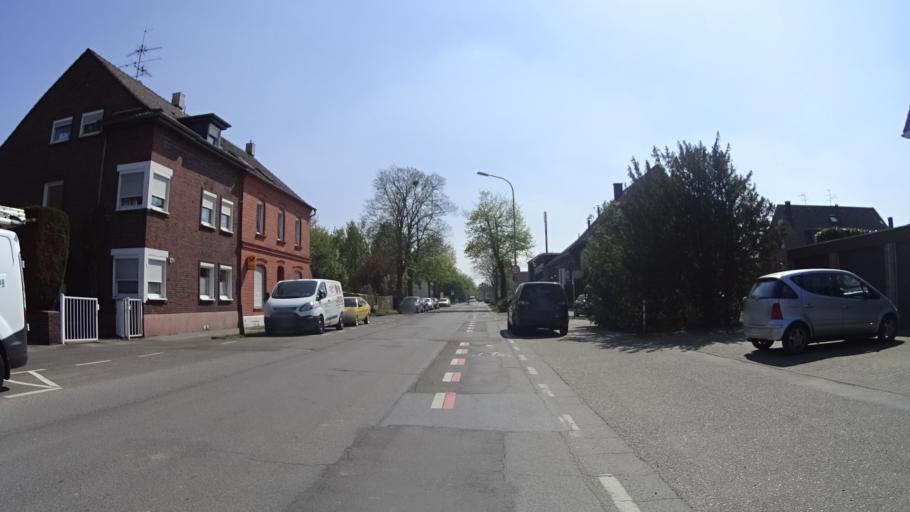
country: DE
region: North Rhine-Westphalia
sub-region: Regierungsbezirk Dusseldorf
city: Meerbusch
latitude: 51.3307
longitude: 6.6698
